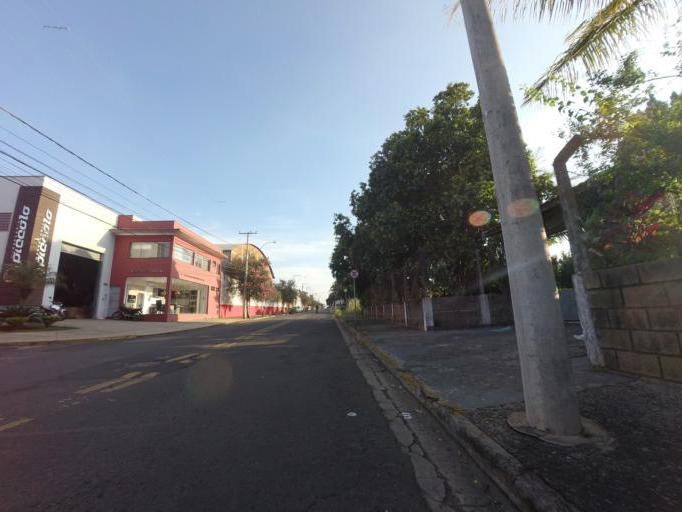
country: BR
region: Sao Paulo
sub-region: Piracicaba
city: Piracicaba
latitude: -22.7393
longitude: -47.6102
